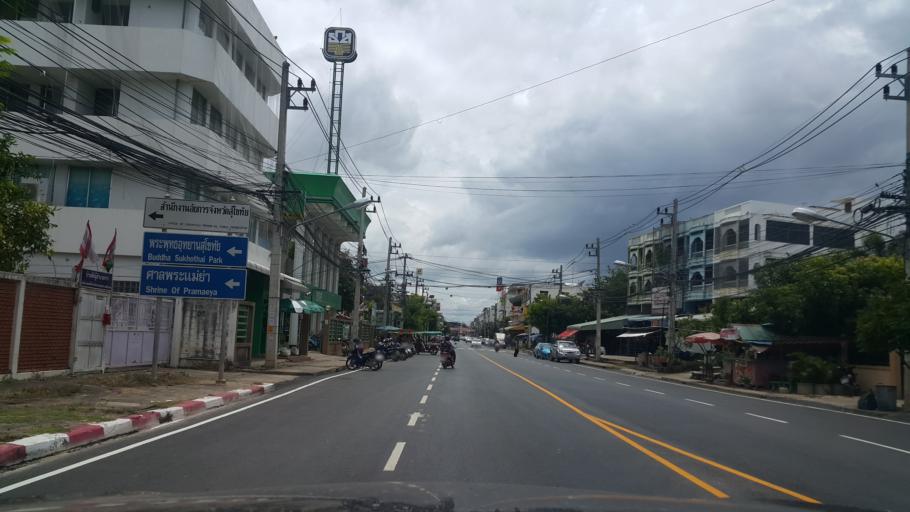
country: TH
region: Sukhothai
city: Sukhothai
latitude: 17.0074
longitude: 99.8245
